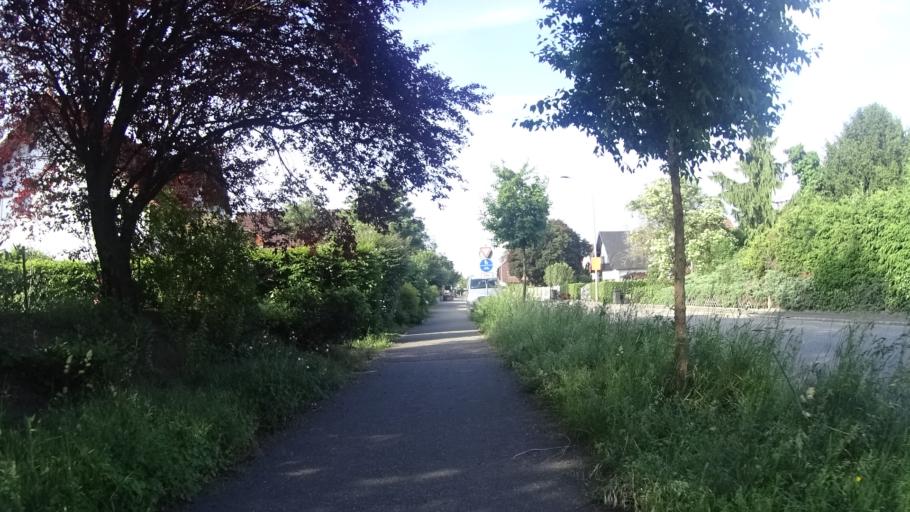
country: DE
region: Baden-Wuerttemberg
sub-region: Freiburg Region
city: Neuenburg am Rhein
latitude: 47.8440
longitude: 7.5785
